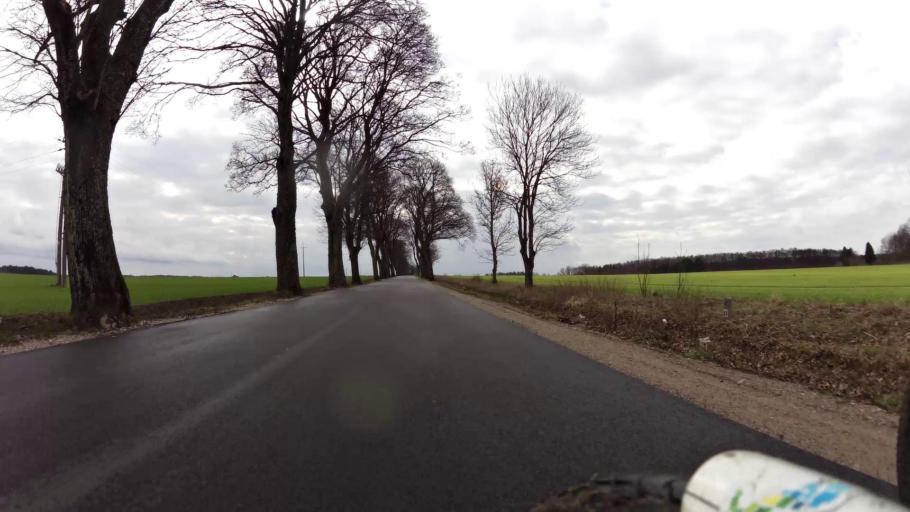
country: PL
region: Pomeranian Voivodeship
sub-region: Powiat bytowski
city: Kolczyglowy
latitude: 54.2356
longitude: 17.2425
